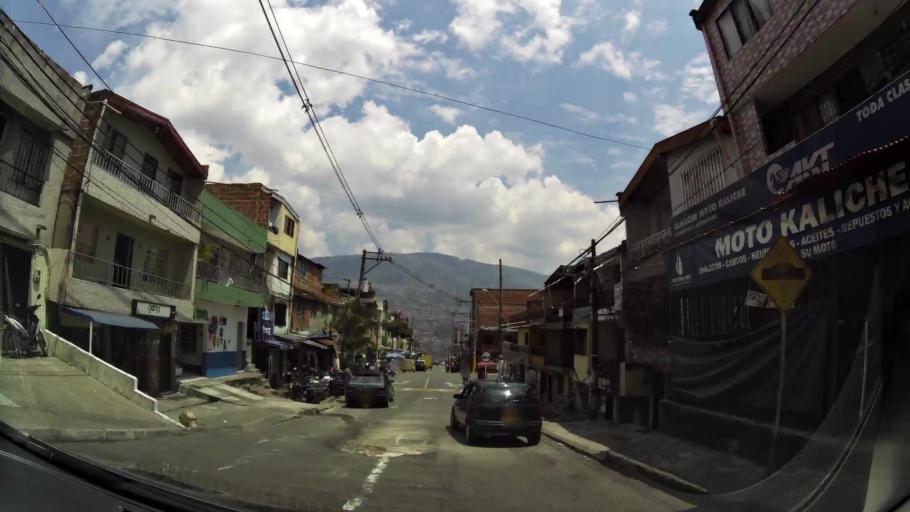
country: CO
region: Antioquia
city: Medellin
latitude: 6.2952
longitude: -75.5756
